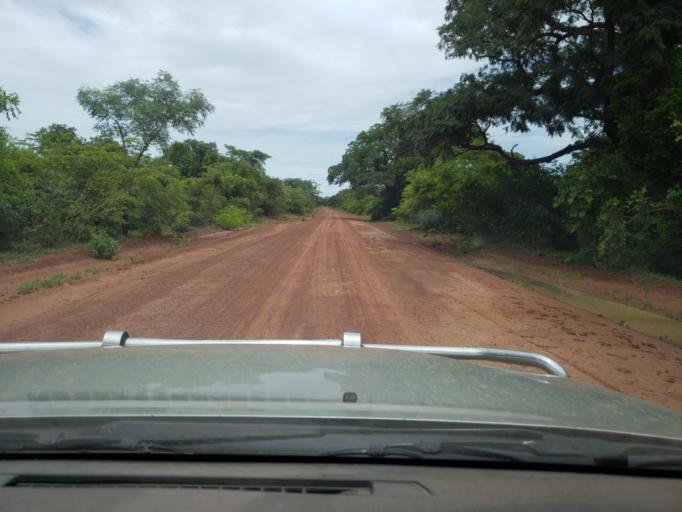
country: ML
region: Sikasso
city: Sikasso
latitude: 11.6638
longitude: -6.3421
